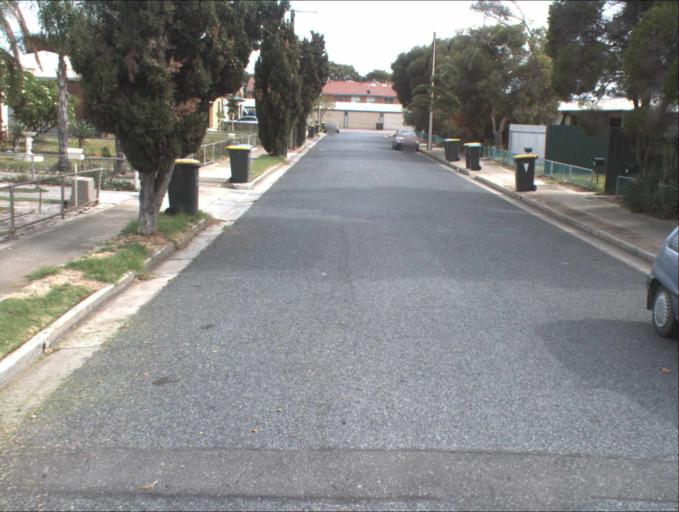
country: AU
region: South Australia
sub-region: Port Adelaide Enfield
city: Birkenhead
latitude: -34.8323
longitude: 138.4986
